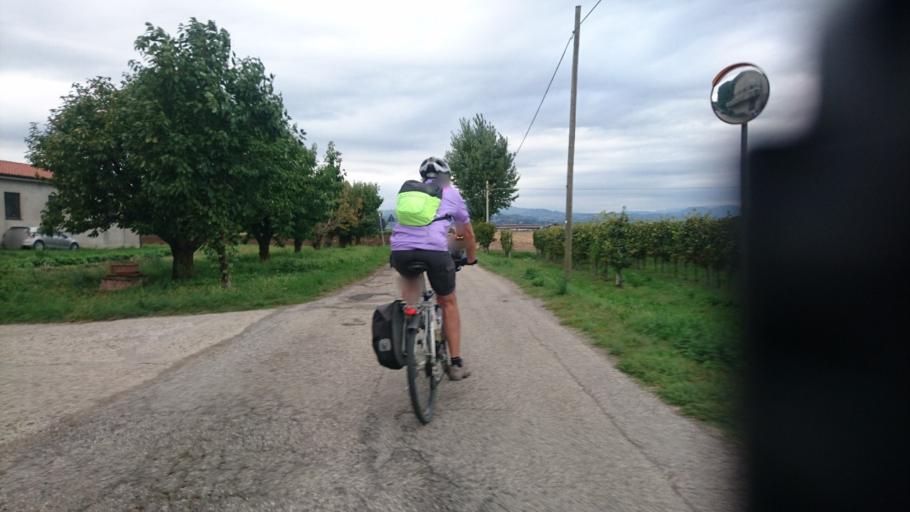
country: IT
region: Veneto
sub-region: Provincia di Vicenza
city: Zermeghedo
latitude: 45.4824
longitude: 11.3814
